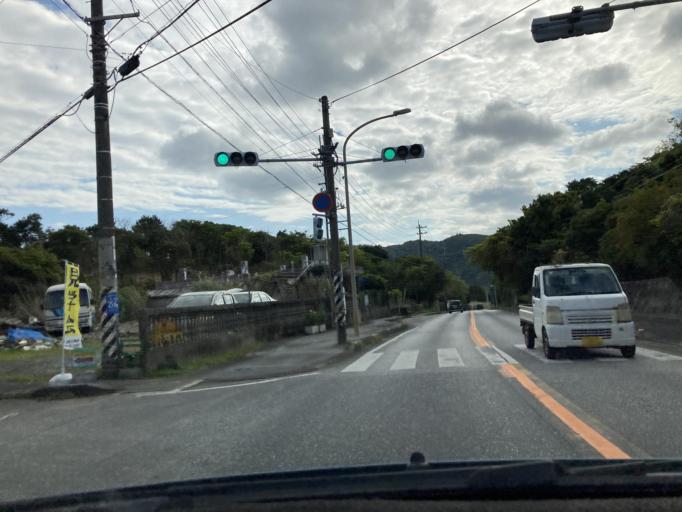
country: JP
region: Okinawa
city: Nago
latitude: 26.6571
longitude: 127.9844
